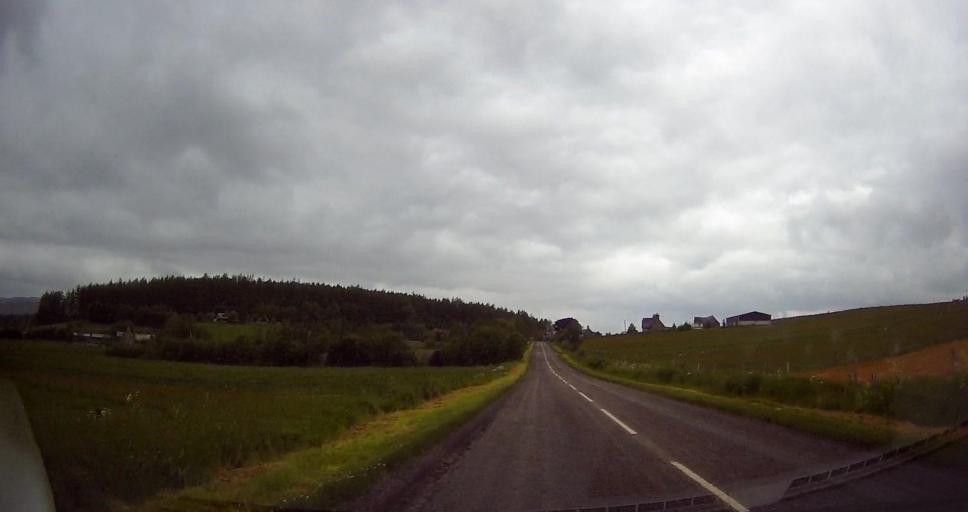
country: GB
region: Scotland
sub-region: Highland
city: Alness
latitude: 58.0197
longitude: -4.3705
